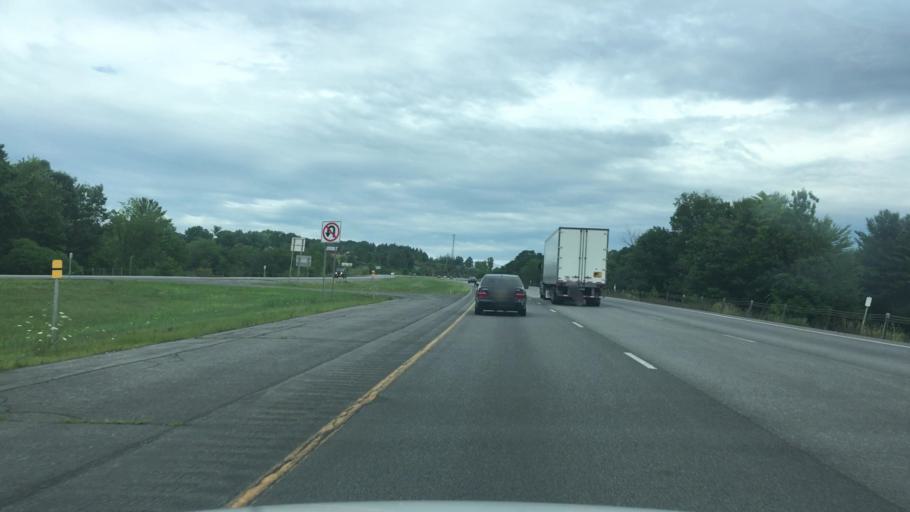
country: US
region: New York
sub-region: Schoharie County
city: Schoharie
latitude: 42.7093
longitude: -74.2997
